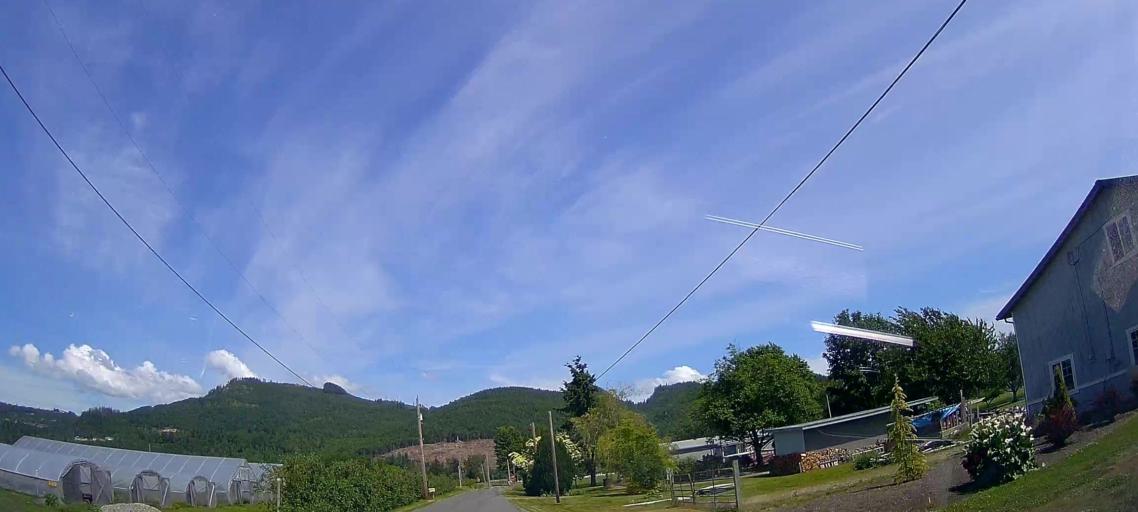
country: US
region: Washington
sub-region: Skagit County
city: Mount Vernon
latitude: 48.3595
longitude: -122.3251
